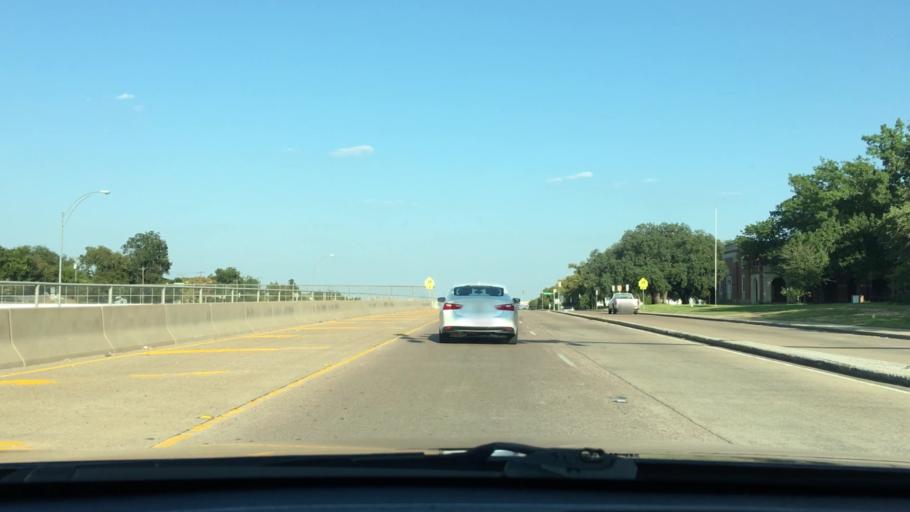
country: US
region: Texas
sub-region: Tarrant County
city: Westworth
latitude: 32.7326
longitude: -97.3868
